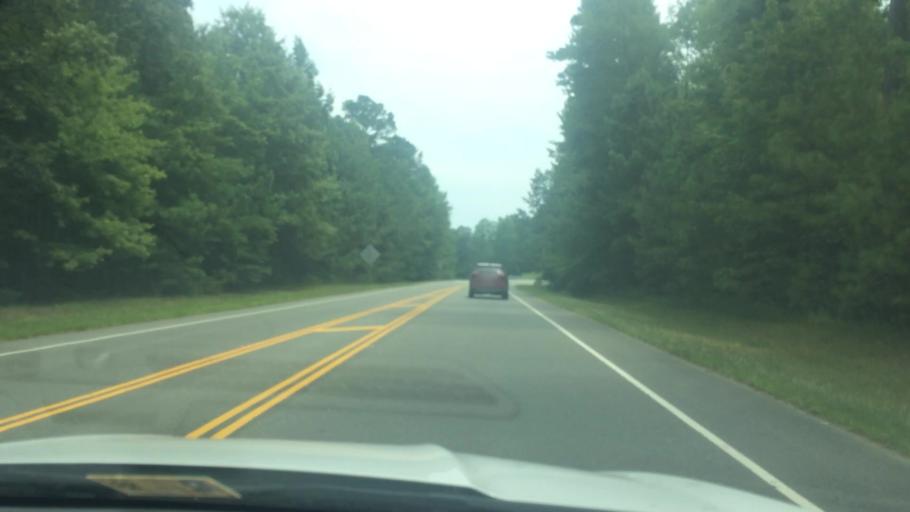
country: US
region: Virginia
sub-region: James City County
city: Williamsburg
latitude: 37.2639
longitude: -76.8034
